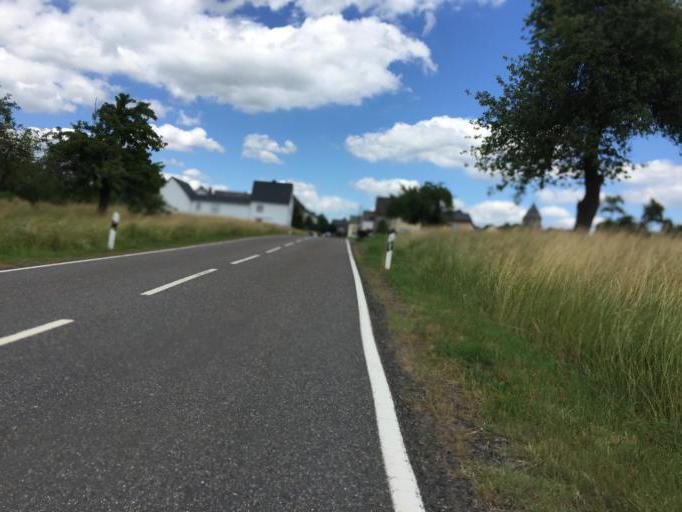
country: DE
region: Rheinland-Pfalz
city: Ruppach-Goldhausen
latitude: 50.4771
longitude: 7.8978
